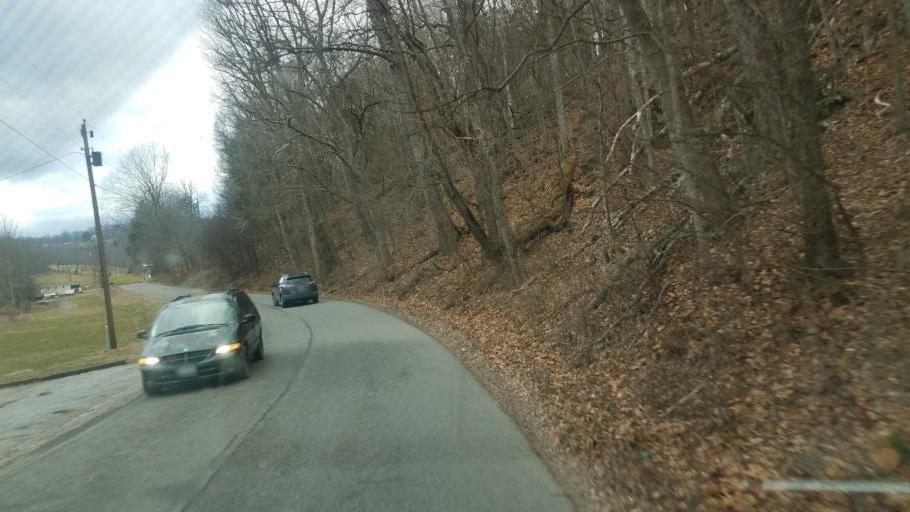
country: US
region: Virginia
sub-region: Giles County
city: Pembroke
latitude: 37.2446
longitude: -80.6773
